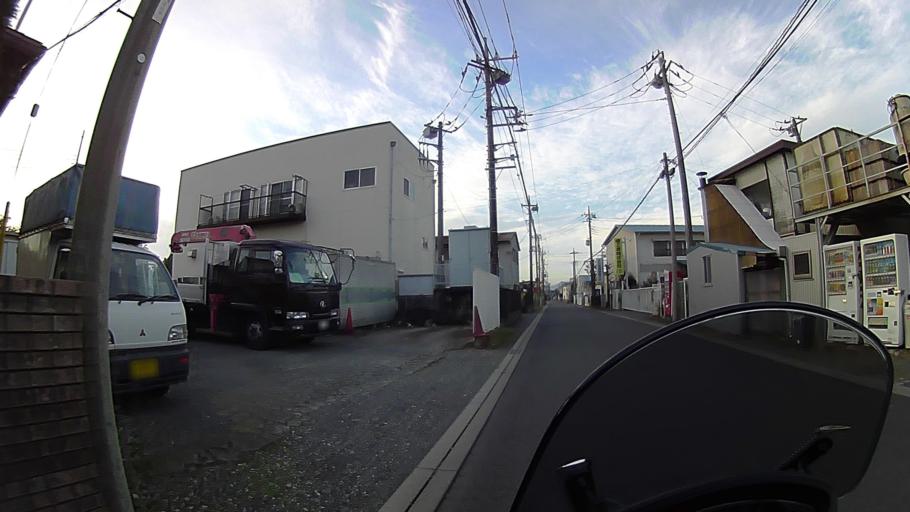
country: JP
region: Kanagawa
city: Atsugi
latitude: 35.4232
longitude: 139.4222
